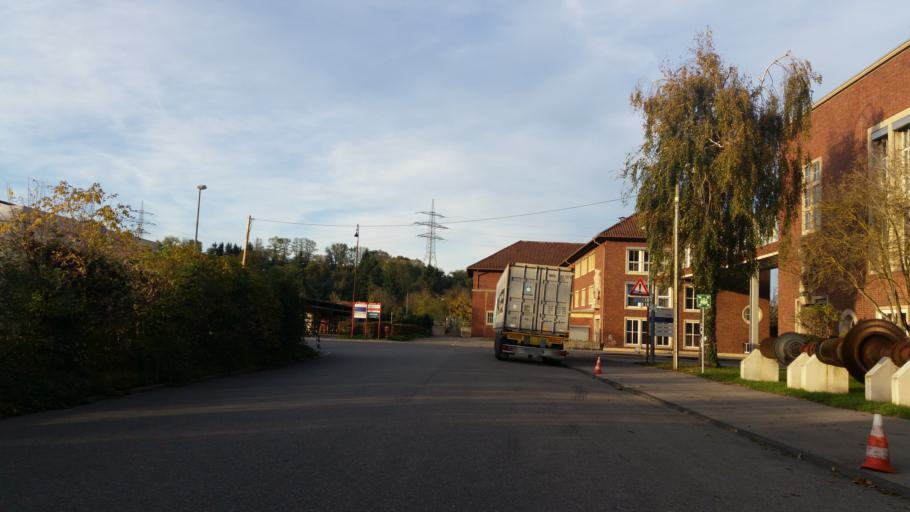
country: DE
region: Baden-Wuerttemberg
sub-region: Regierungsbezirk Stuttgart
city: Benningen am Neckar
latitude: 48.9273
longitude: 9.2372
